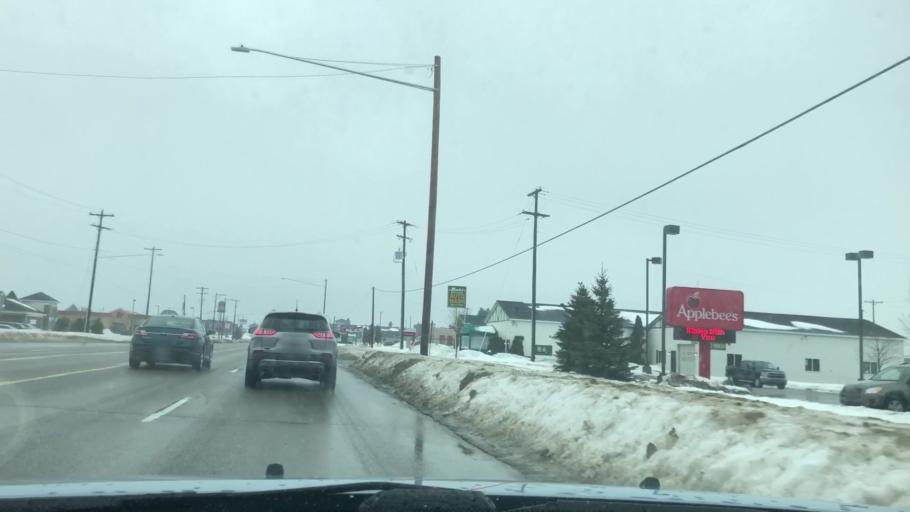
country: US
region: Michigan
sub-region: Otsego County
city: Gaylord
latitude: 45.0274
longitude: -84.6989
